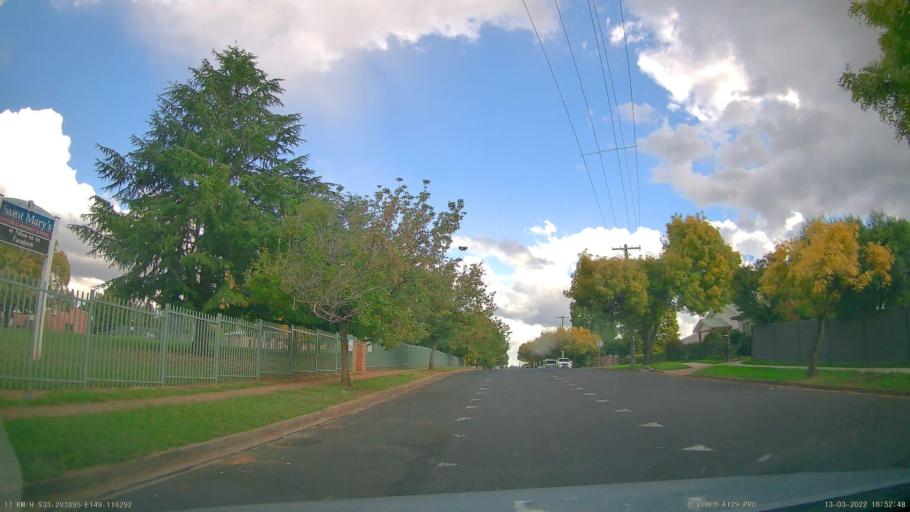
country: AU
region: New South Wales
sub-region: Orange Municipality
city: Orange
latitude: -33.2840
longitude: 149.1163
